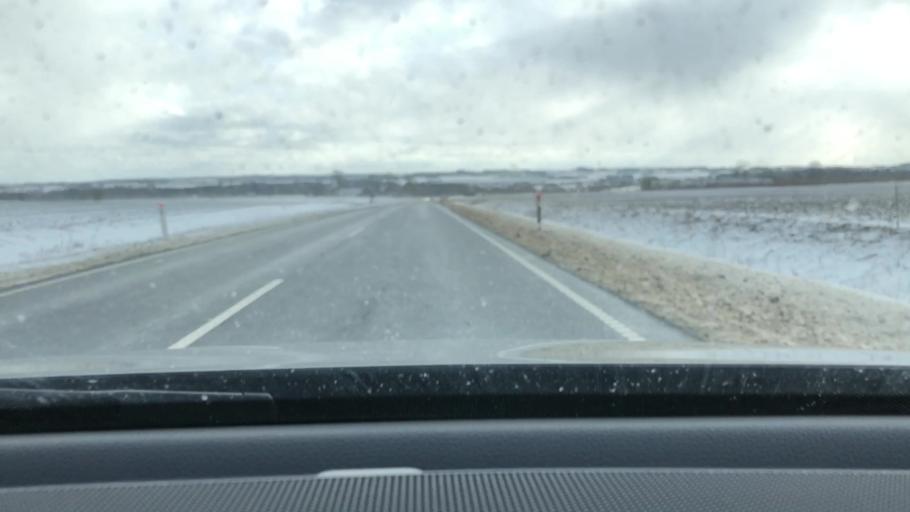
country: DK
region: Central Jutland
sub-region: Skanderborg Kommune
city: Galten
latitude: 56.1836
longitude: 9.8491
